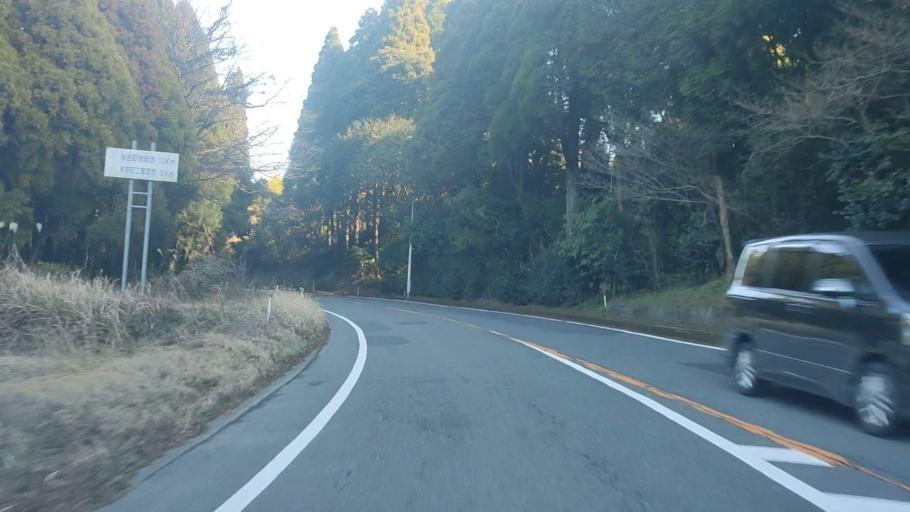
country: JP
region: Kagoshima
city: Sueyoshicho-ninokata
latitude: 31.6727
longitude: 130.9239
